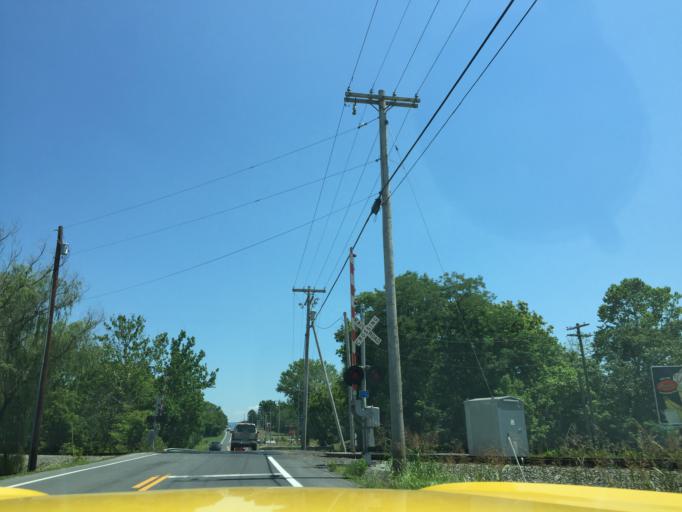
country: US
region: West Virginia
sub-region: Jefferson County
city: Ranson
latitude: 39.2970
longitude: -77.9002
